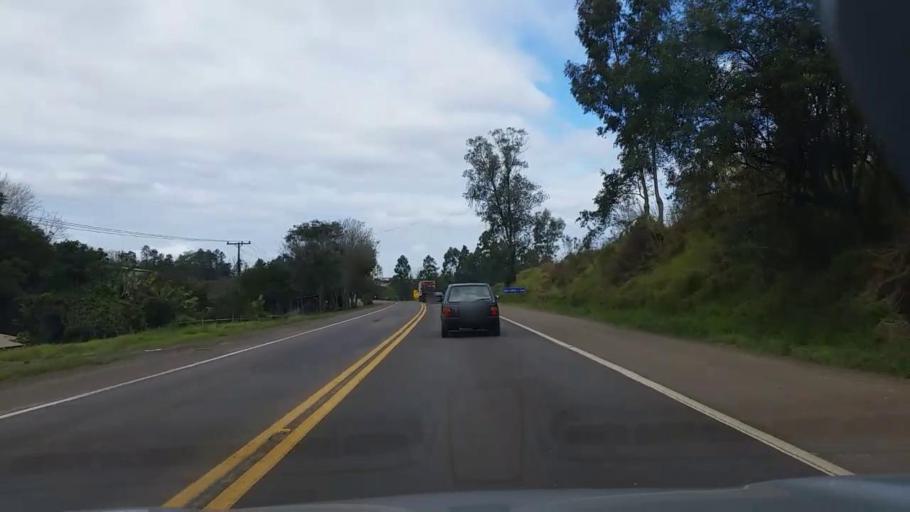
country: BR
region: Rio Grande do Sul
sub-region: Lajeado
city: Lajeado
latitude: -29.4238
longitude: -52.0211
